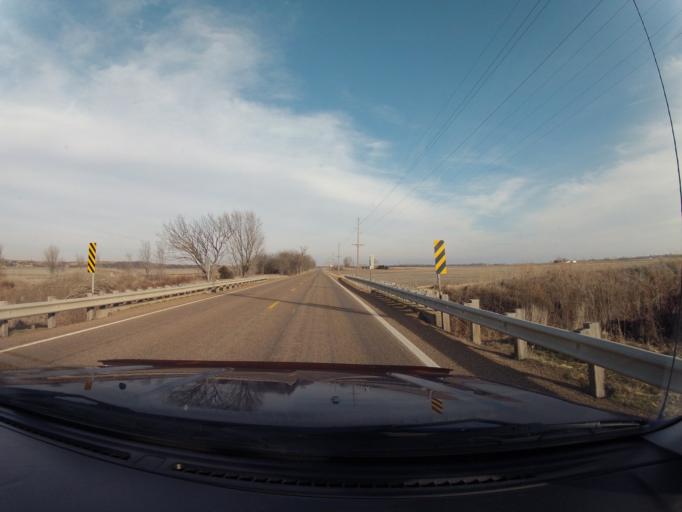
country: US
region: Kansas
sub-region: Pottawatomie County
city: Saint Marys
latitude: 39.2165
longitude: -96.1586
